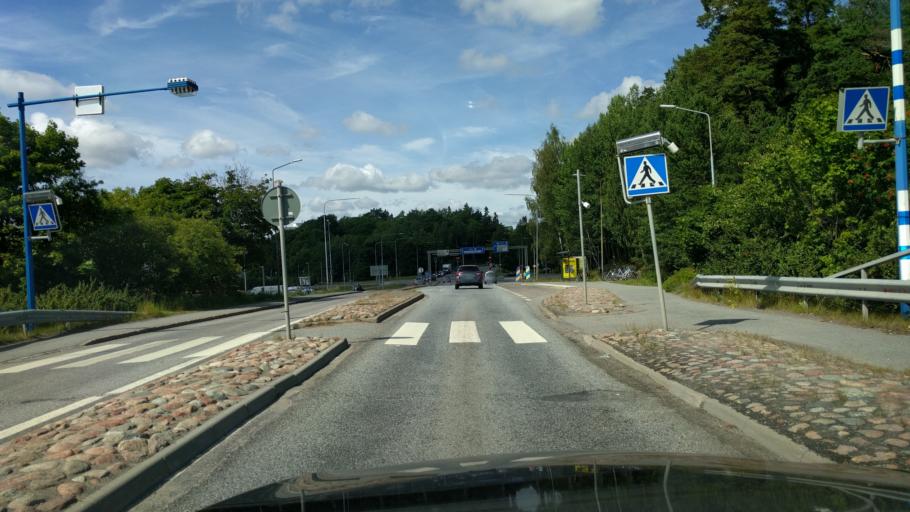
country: SE
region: Stockholm
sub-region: Taby Kommun
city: Taby
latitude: 59.4345
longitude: 18.0691
